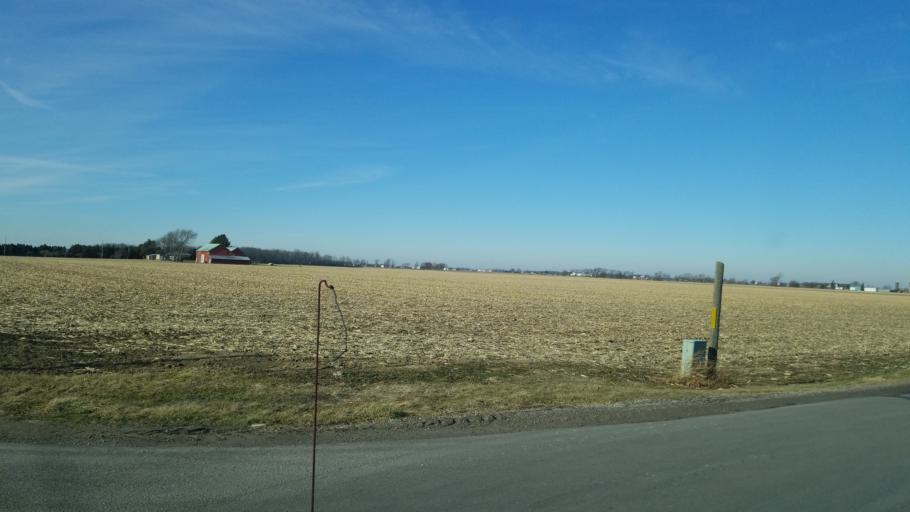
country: US
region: Ohio
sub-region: Putnam County
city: Leipsic
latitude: 41.1237
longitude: -83.9769
